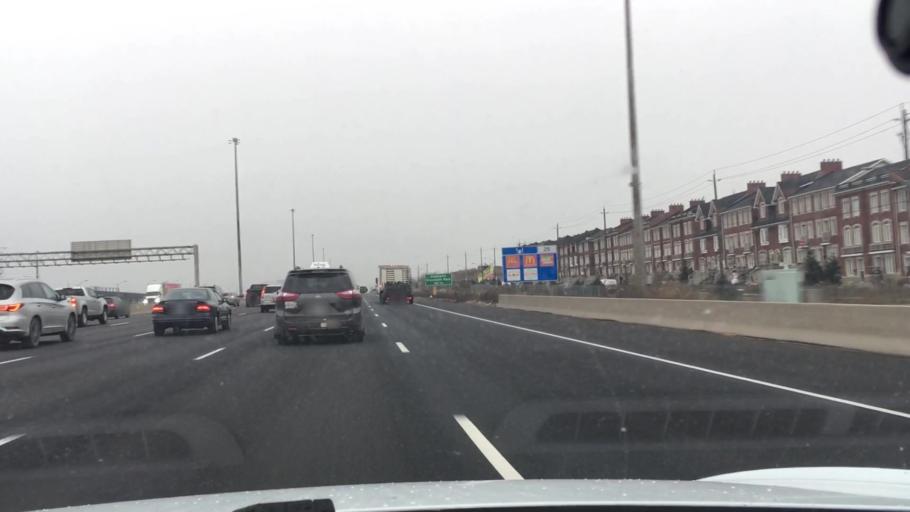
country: CA
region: Ontario
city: Concord
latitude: 43.7274
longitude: -79.5241
